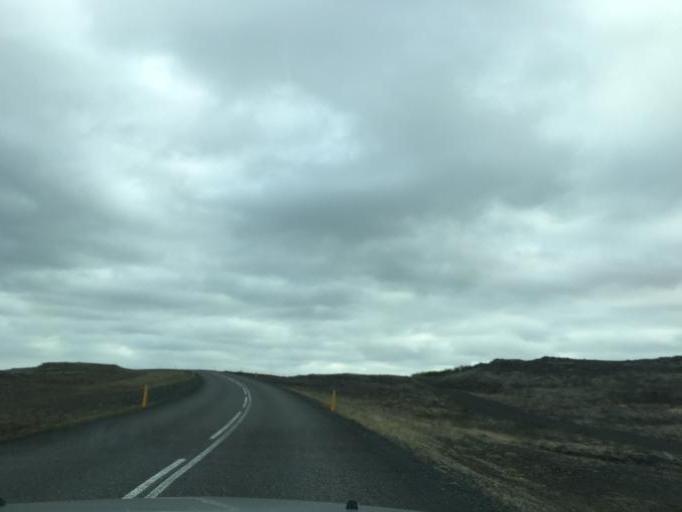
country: IS
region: South
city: Vestmannaeyjar
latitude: 64.2478
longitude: -20.2083
